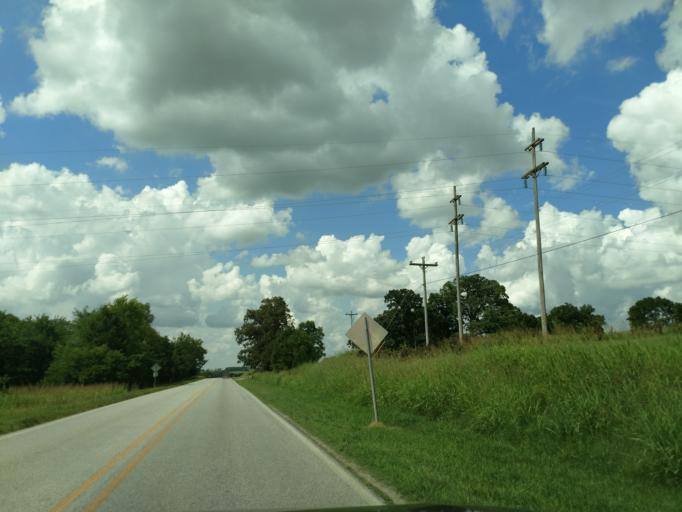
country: US
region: Arkansas
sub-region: Carroll County
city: Berryville
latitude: 36.3943
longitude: -93.5661
